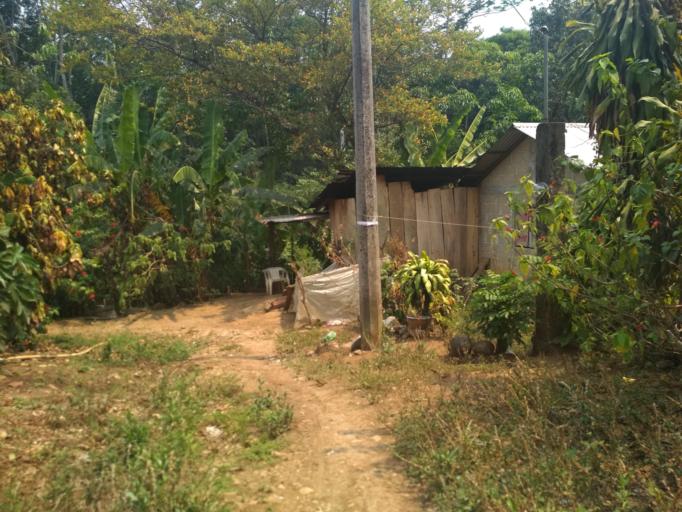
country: MX
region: Veracruz
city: Cosolapa
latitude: 18.5876
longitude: -96.7137
